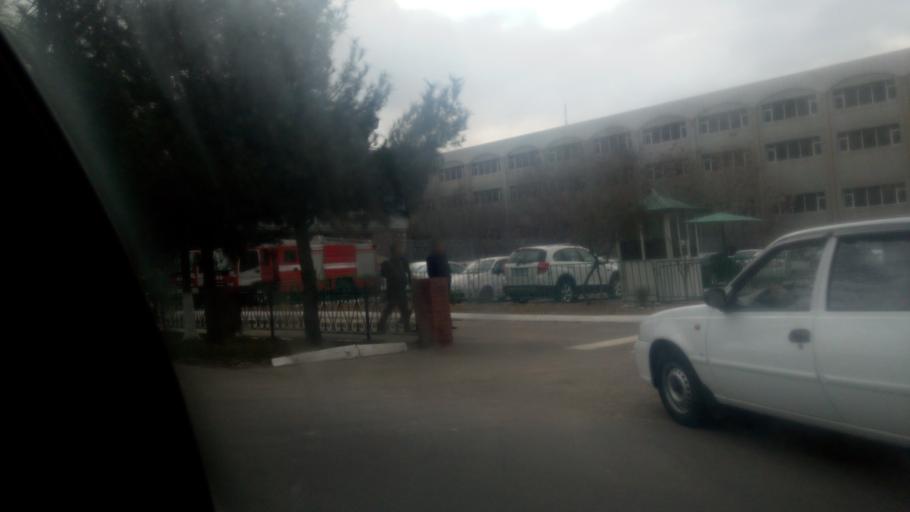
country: UZ
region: Toshkent Shahri
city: Tashkent
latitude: 41.3351
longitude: 69.2846
